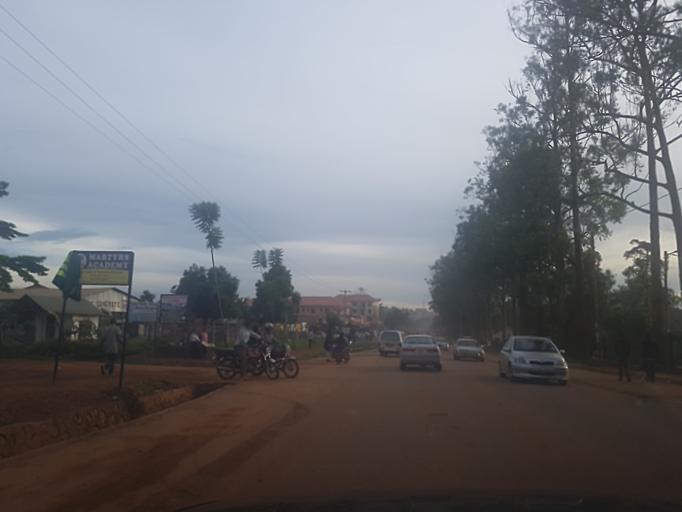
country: UG
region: Central Region
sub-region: Wakiso District
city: Bweyogerere
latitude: 0.3875
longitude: 32.6543
